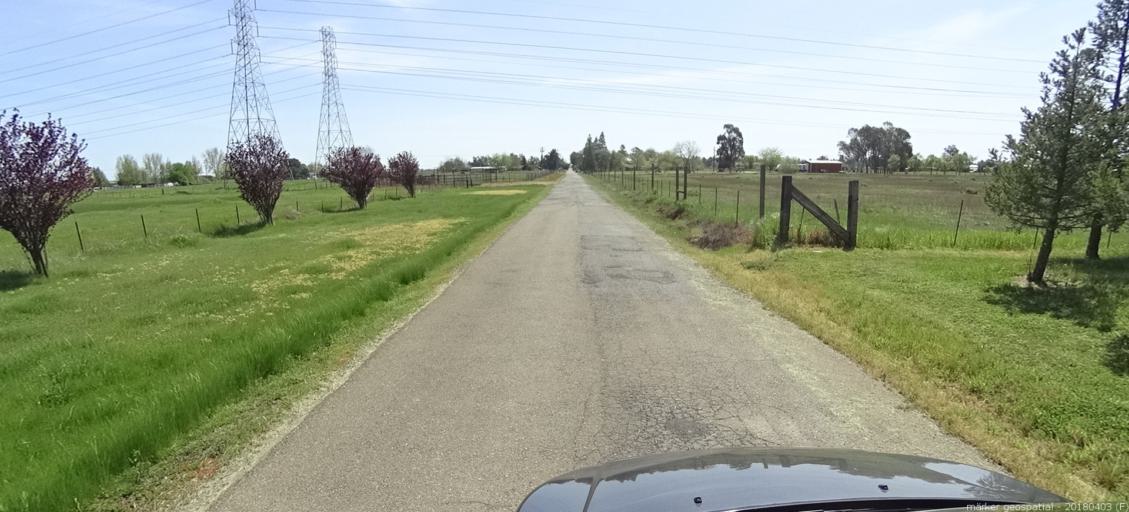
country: US
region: California
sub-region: Sacramento County
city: Clay
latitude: 38.3530
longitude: -121.2147
